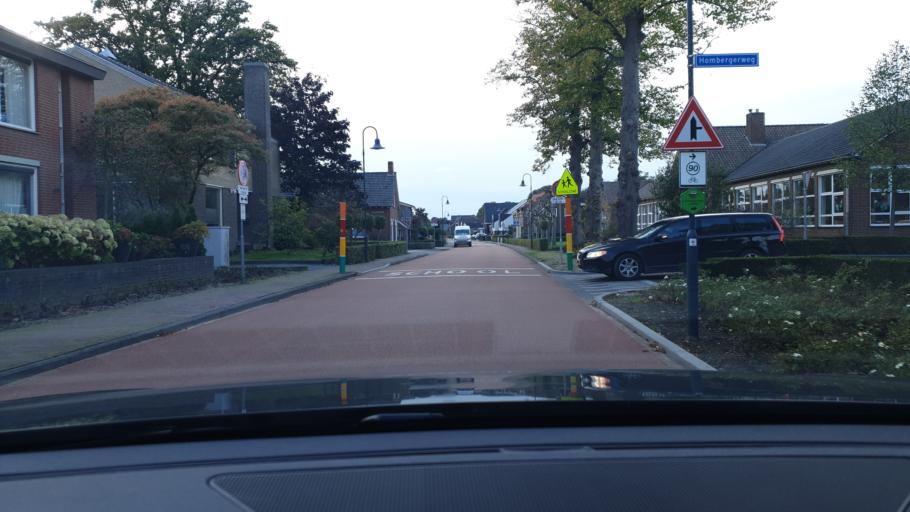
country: NL
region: Limburg
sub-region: Gemeente Venlo
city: Arcen
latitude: 51.4620
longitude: 6.1612
